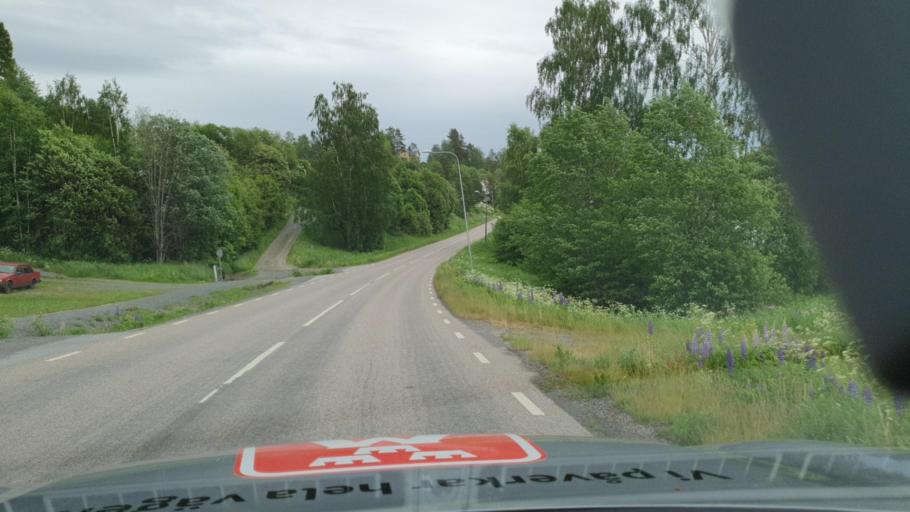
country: SE
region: Vaesternorrland
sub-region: Kramfors Kommun
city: Nordingra
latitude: 62.9325
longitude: 18.2707
